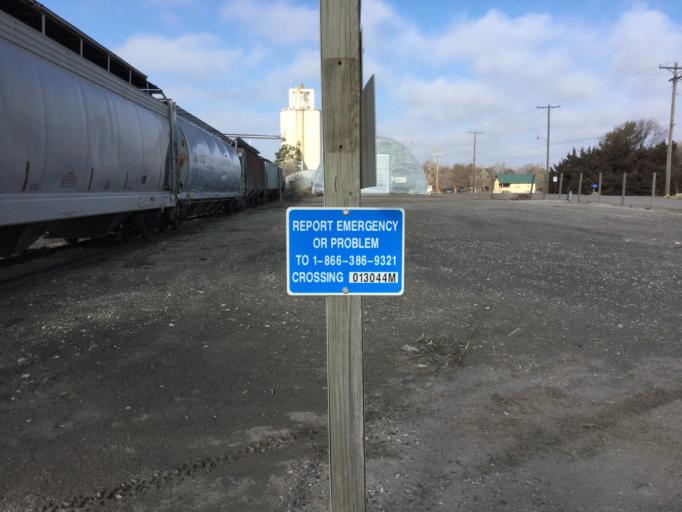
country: US
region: Kansas
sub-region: Scott County
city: Scott City
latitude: 38.4880
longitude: -100.9071
